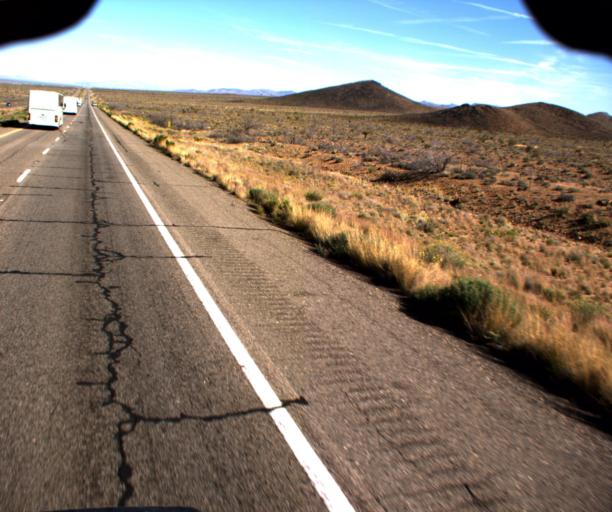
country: US
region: Arizona
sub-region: Mohave County
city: Dolan Springs
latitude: 35.4492
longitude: -114.2966
